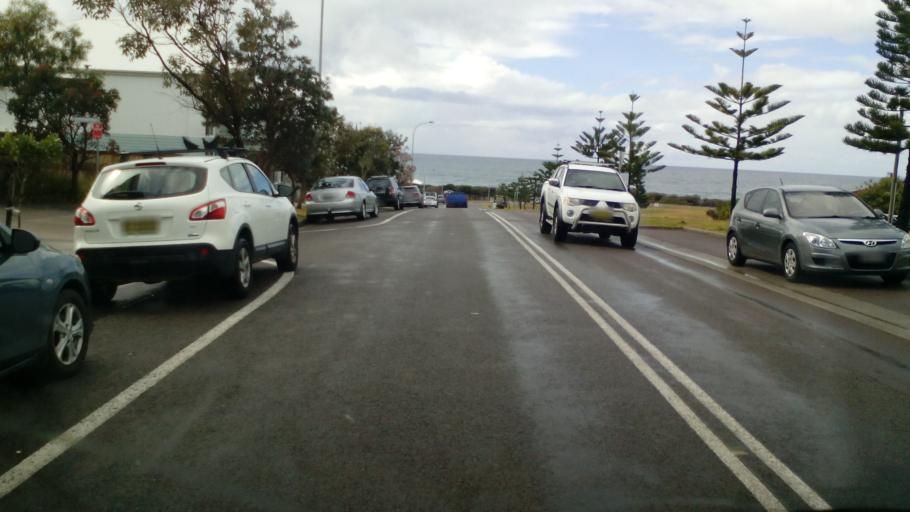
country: AU
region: New South Wales
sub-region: Lake Macquarie Shire
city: Belmont South
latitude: -33.1049
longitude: 151.6456
